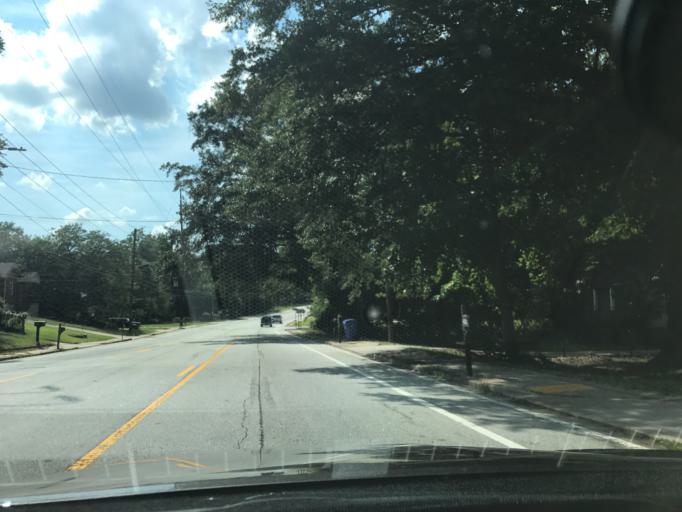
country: US
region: Georgia
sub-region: DeKalb County
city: Candler-McAfee
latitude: 33.7390
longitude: -84.2922
